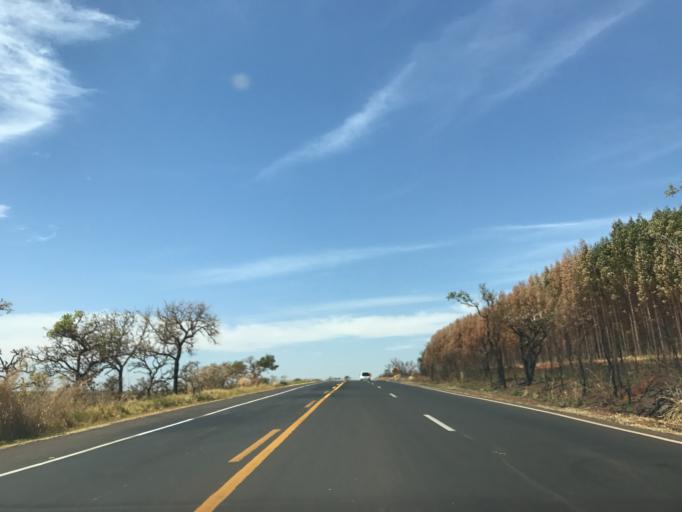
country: BR
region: Minas Gerais
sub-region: Prata
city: Prata
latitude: -19.1217
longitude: -48.9681
